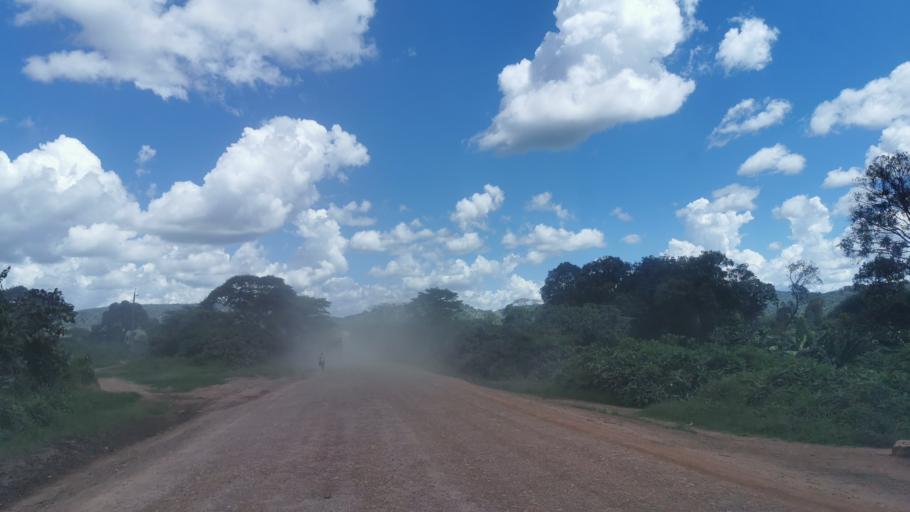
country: TZ
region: Kagera
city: Biharamulo
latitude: -2.8897
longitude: 31.1400
